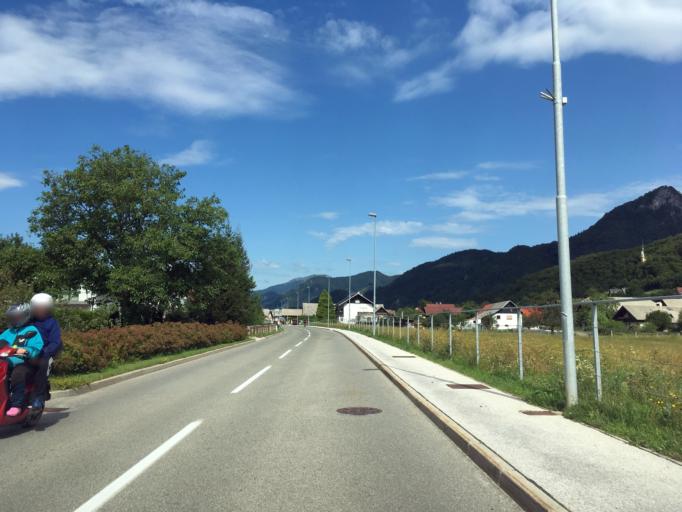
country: SI
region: Zirovnica
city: Zirovnica
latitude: 46.4018
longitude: 14.1396
